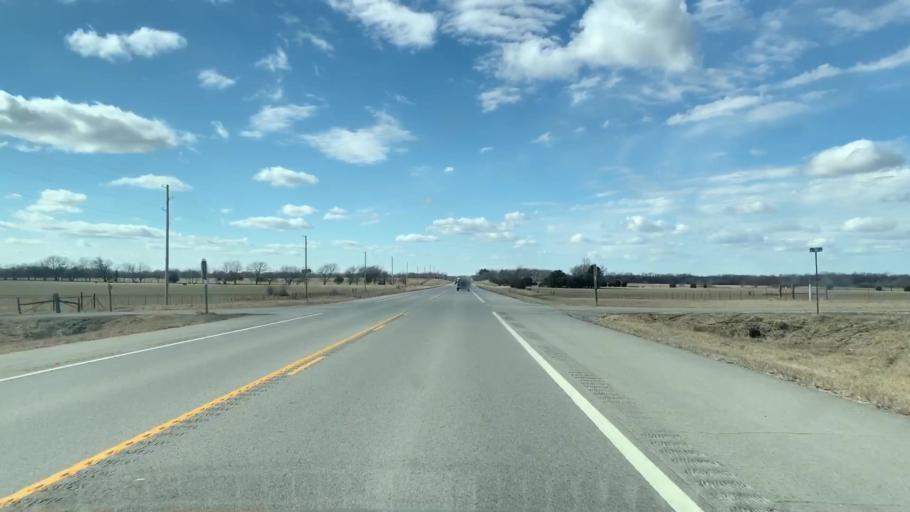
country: US
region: Kansas
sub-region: Labette County
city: Oswego
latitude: 37.3401
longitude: -95.0491
